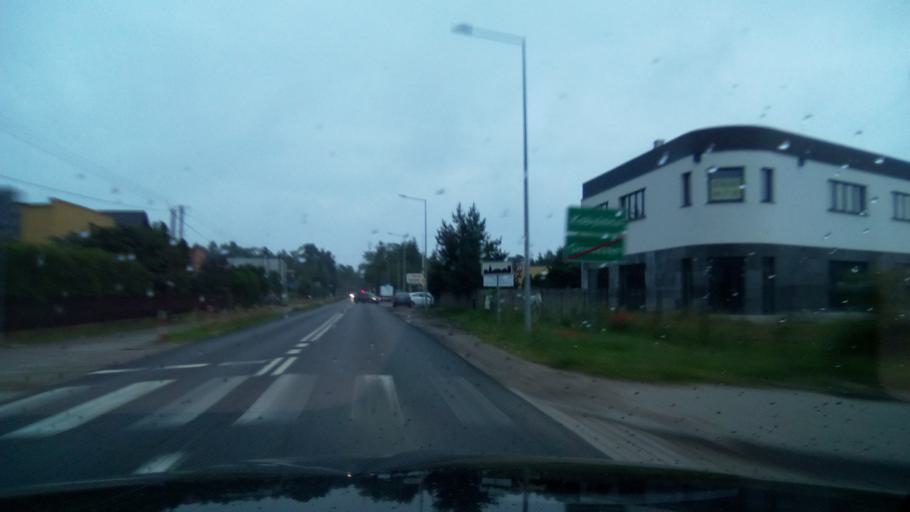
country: PL
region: Greater Poland Voivodeship
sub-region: Powiat poznanski
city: Kobylnica
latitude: 52.4418
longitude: 17.0755
